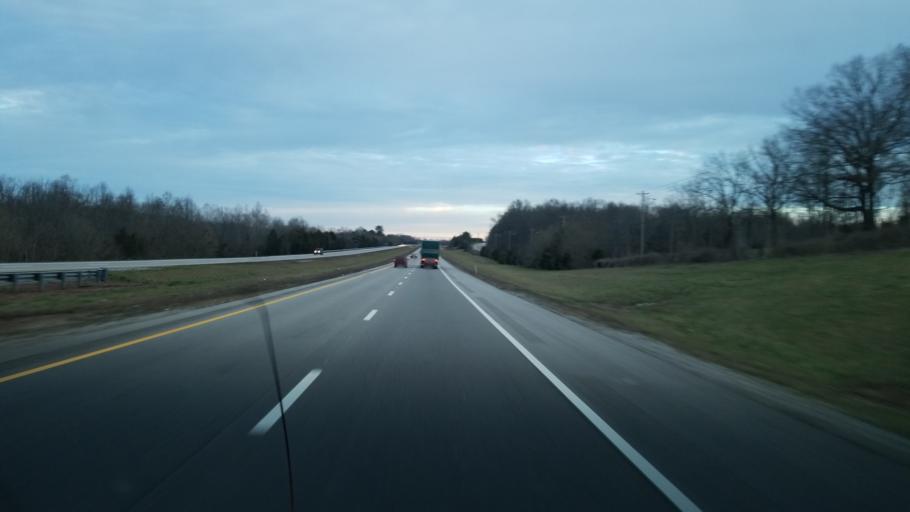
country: US
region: Tennessee
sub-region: Putnam County
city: Cookeville
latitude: 36.0878
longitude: -85.5057
